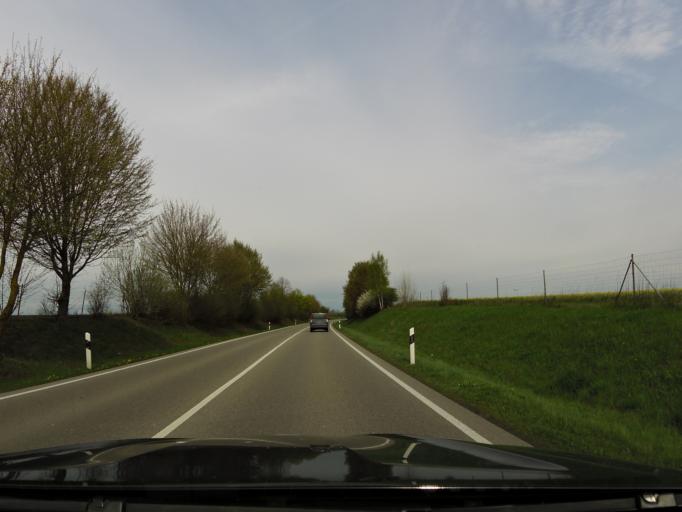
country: DE
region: Bavaria
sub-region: Upper Bavaria
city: Oberding
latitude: 48.3392
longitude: 11.8593
